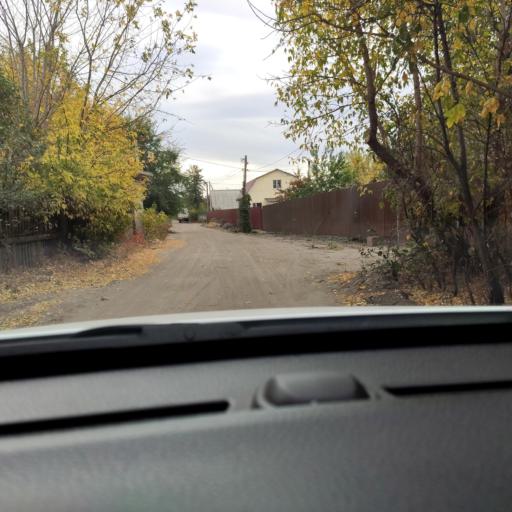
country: RU
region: Voronezj
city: Maslovka
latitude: 51.6059
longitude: 39.2788
